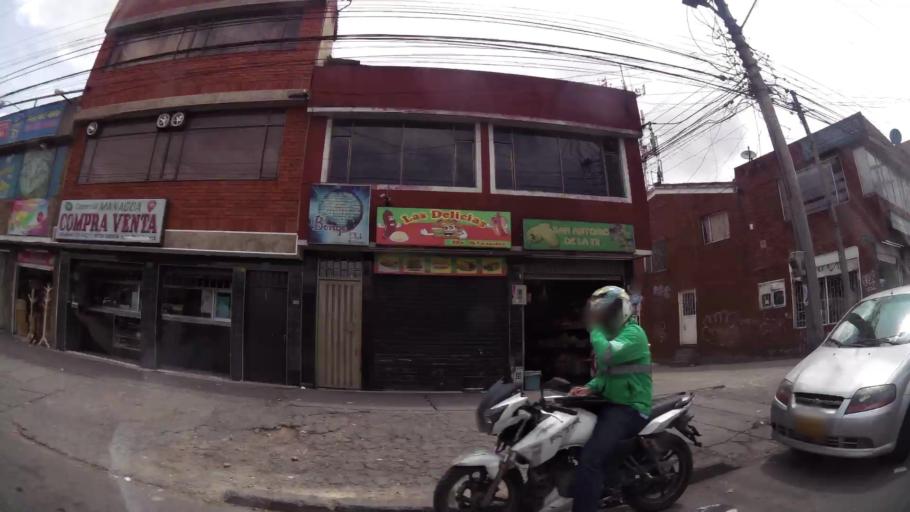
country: CO
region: Bogota D.C.
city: Bogota
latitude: 4.7023
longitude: -74.1146
